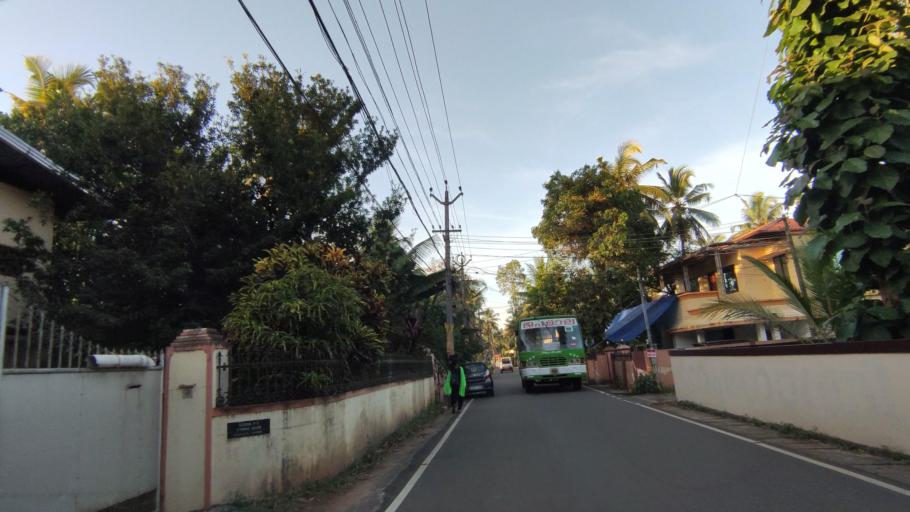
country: IN
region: Kerala
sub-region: Kottayam
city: Kottayam
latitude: 9.6158
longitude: 76.4937
